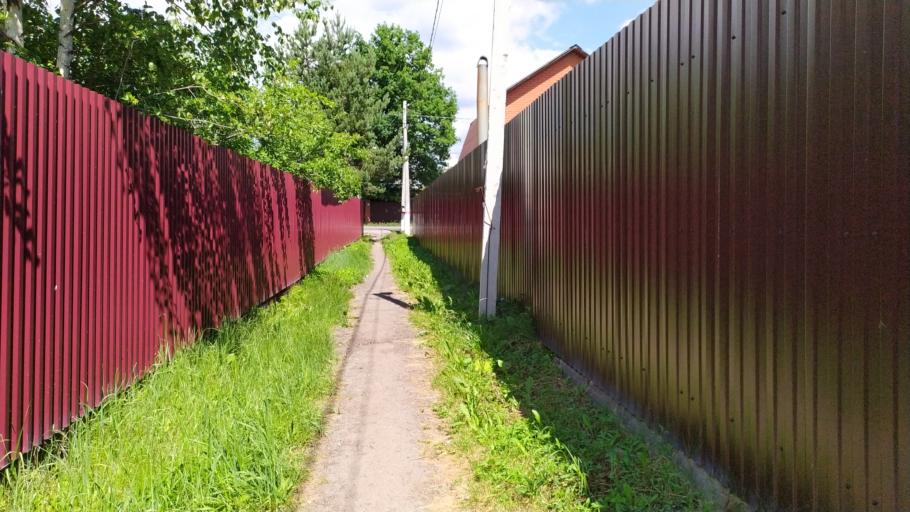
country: RU
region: Moskovskaya
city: Kratovo
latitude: 55.6370
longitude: 38.1701
